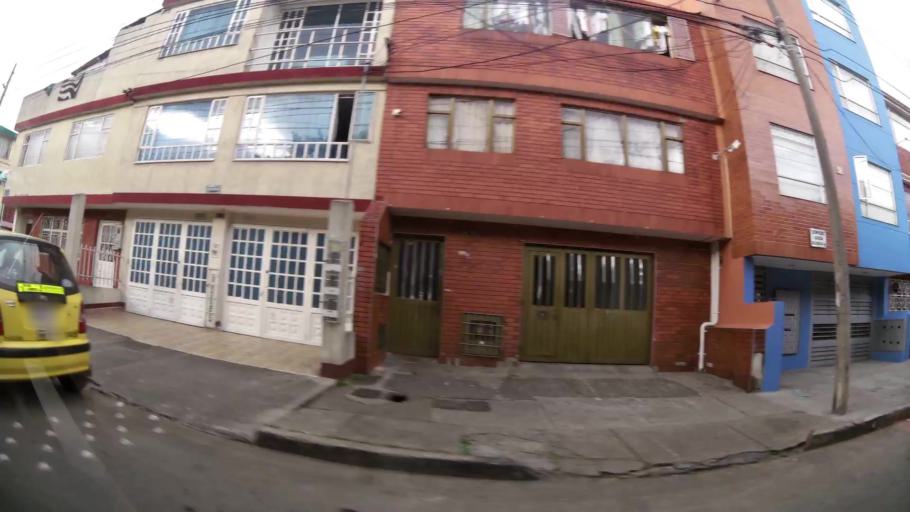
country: CO
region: Bogota D.C.
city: Bogota
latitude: 4.6111
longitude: -74.1122
